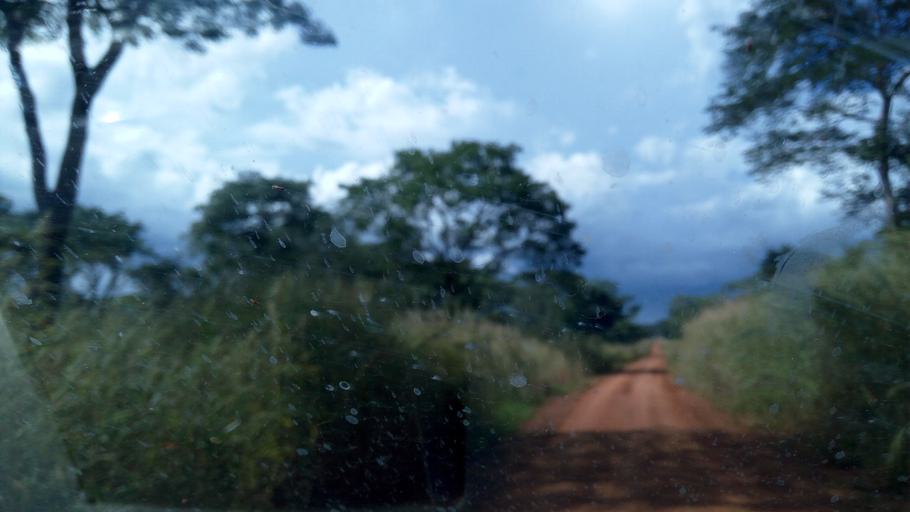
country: ZM
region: Northern
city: Kaputa
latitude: -8.1594
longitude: 29.0992
